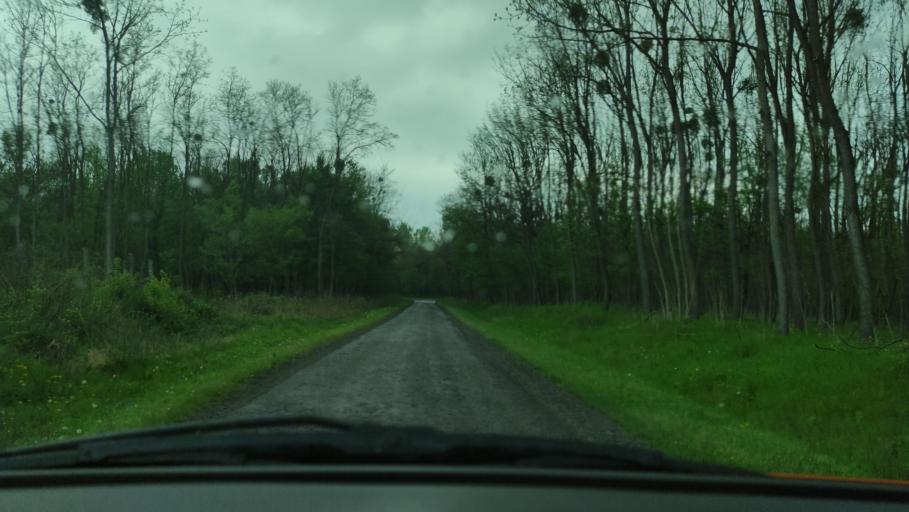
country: HU
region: Baranya
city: Mohacs
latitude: 45.9104
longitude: 18.7530
